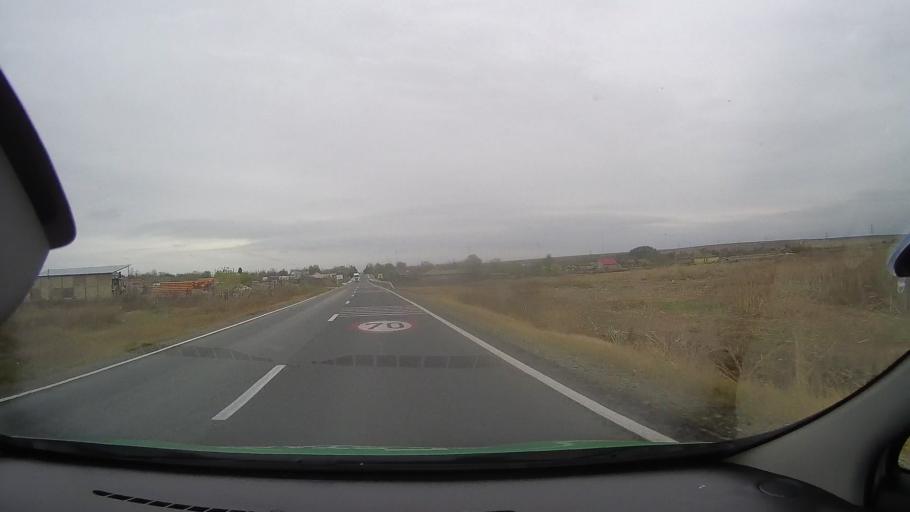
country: RO
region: Constanta
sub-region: Comuna Nicolae Balcescu
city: Dorobantu
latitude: 44.4134
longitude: 28.3192
